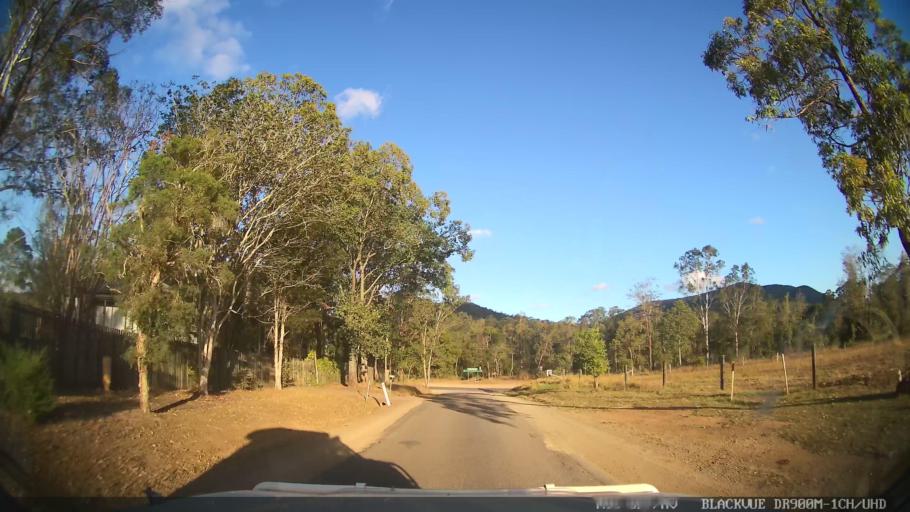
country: AU
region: Queensland
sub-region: Sunshine Coast
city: Nambour
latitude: -26.6281
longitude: 152.6859
